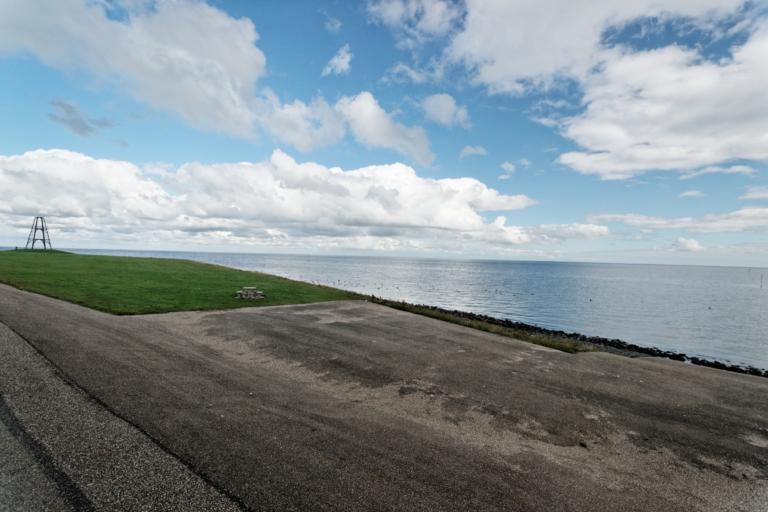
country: NL
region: North Holland
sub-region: Gemeente Texel
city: Den Burg
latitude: 53.0768
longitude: 4.8936
